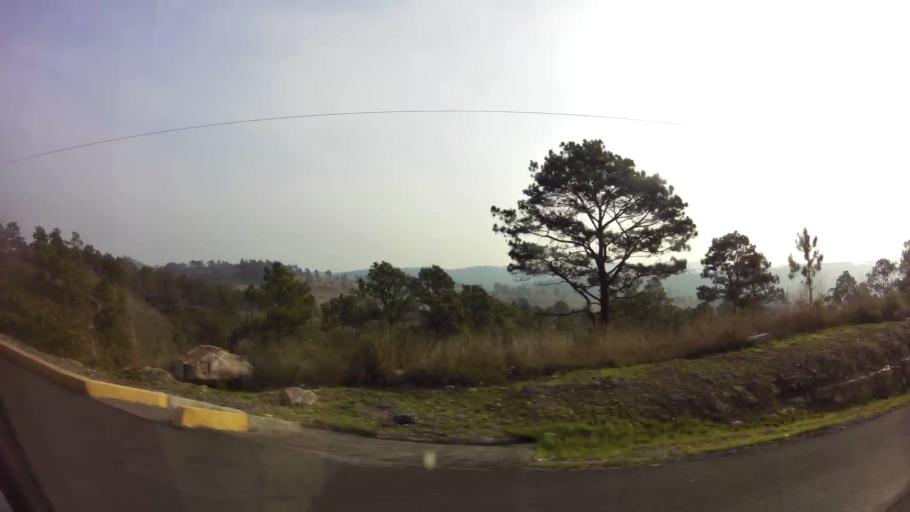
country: HN
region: Francisco Morazan
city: Zambrano
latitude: 14.2525
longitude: -87.3832
